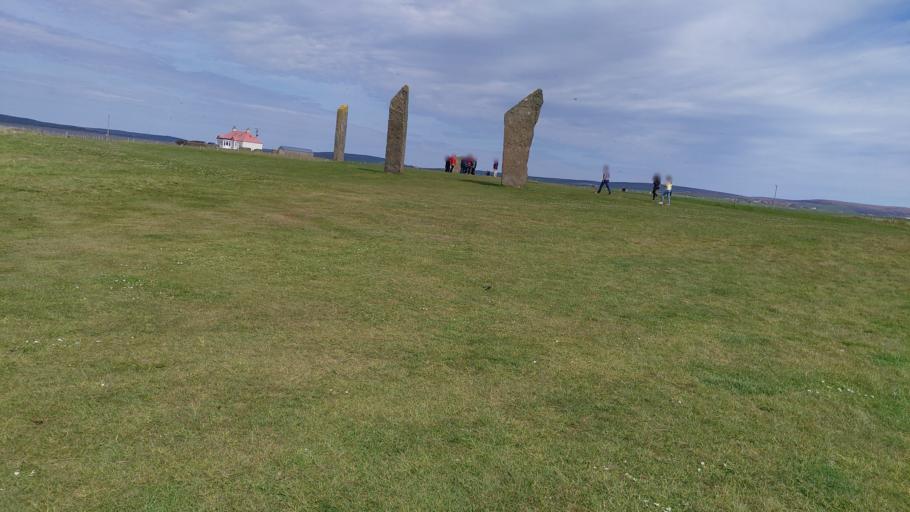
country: GB
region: Scotland
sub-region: Orkney Islands
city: Stromness
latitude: 58.9935
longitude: -3.2082
